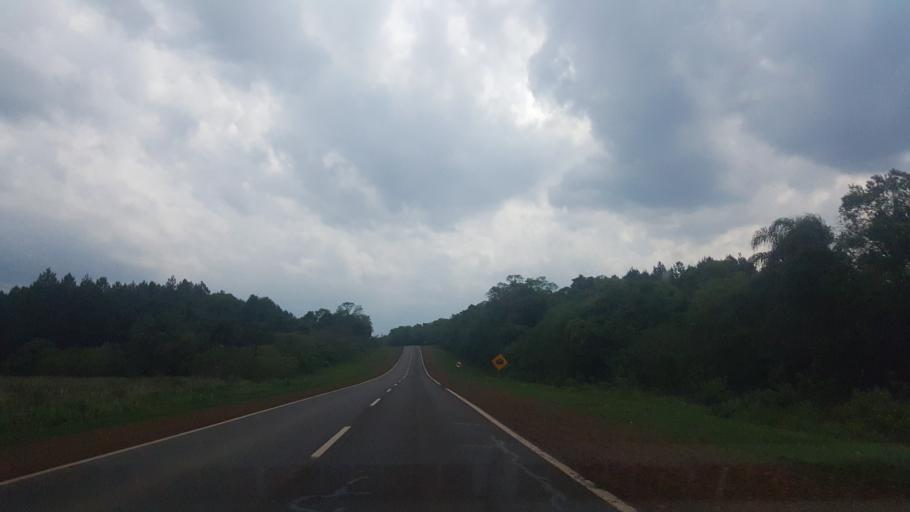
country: AR
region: Misiones
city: Santo Pipo
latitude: -27.1142
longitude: -55.3585
